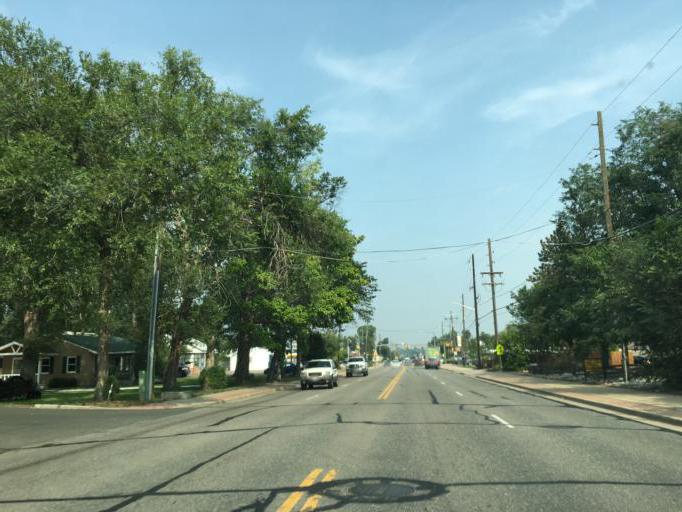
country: US
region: Colorado
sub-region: Jefferson County
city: Arvada
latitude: 39.7781
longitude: -105.1125
